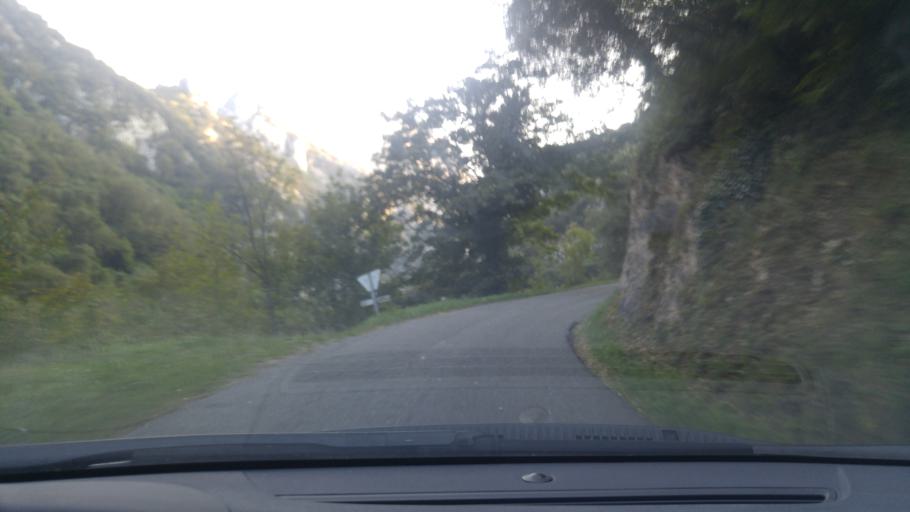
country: ES
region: Asturias
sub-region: Province of Asturias
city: Proaza
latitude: 43.2485
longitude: -6.0244
